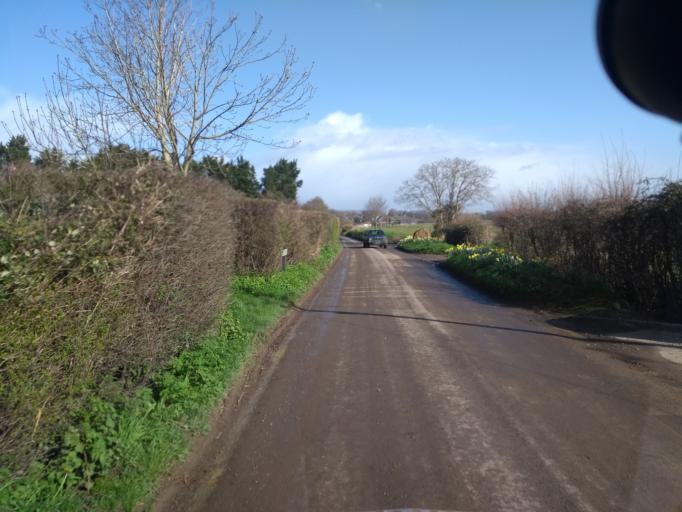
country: GB
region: England
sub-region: Somerset
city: South Petherton
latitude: 50.9548
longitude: -2.8420
